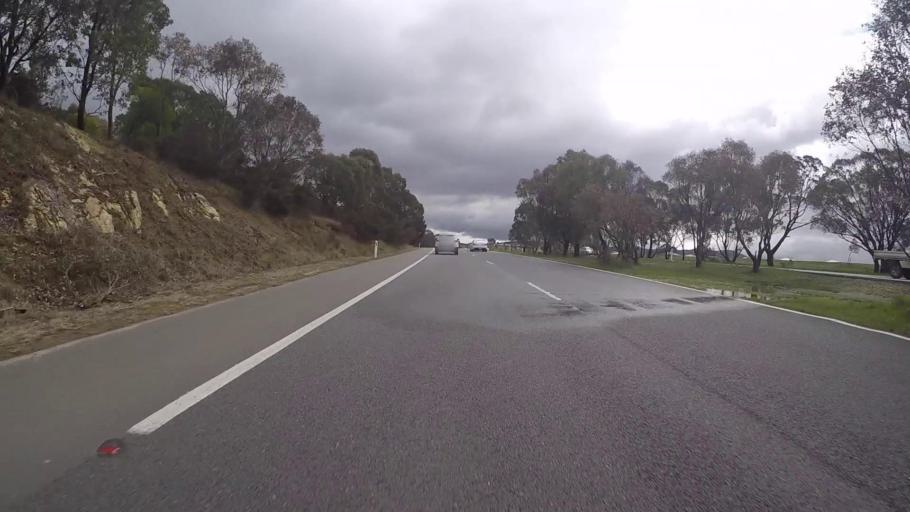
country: AU
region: Australian Capital Territory
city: Kaleen
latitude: -35.2100
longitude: 149.1089
